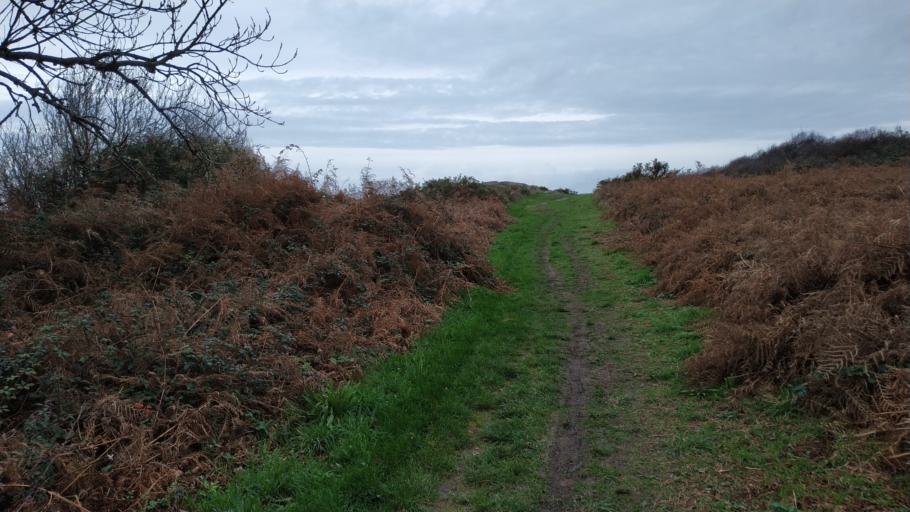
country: ES
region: Galicia
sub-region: Provincia da Coruna
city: Oleiros
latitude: 43.3999
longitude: -8.3296
